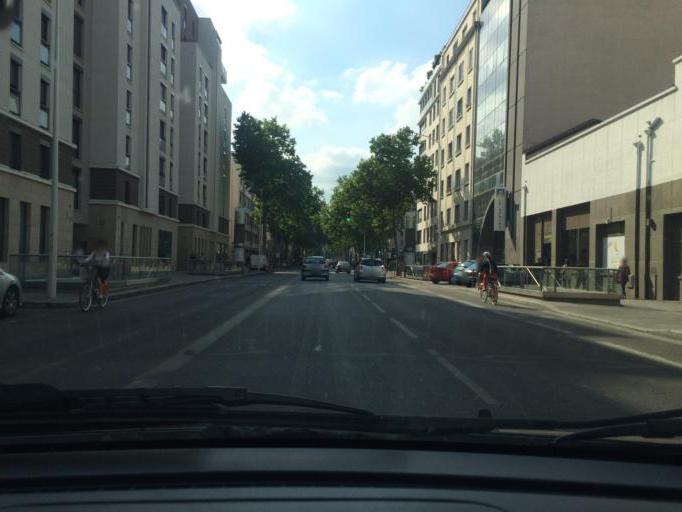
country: FR
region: Rhone-Alpes
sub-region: Departement du Rhone
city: Lyon
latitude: 45.7476
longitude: 4.8653
